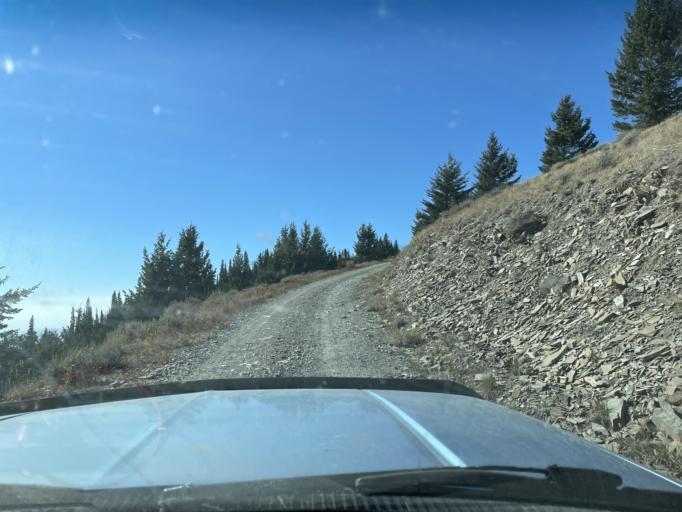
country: US
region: Montana
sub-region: Broadwater County
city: Townsend
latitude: 46.4975
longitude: -111.2621
